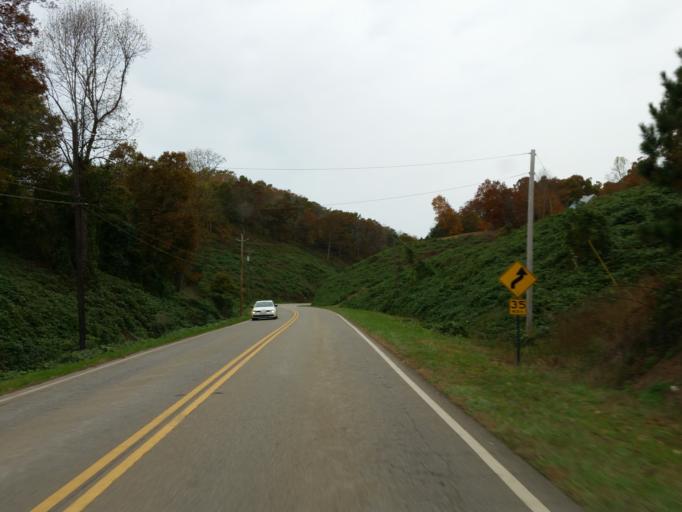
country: US
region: Georgia
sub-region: Pickens County
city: Jasper
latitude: 34.4962
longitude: -84.4307
